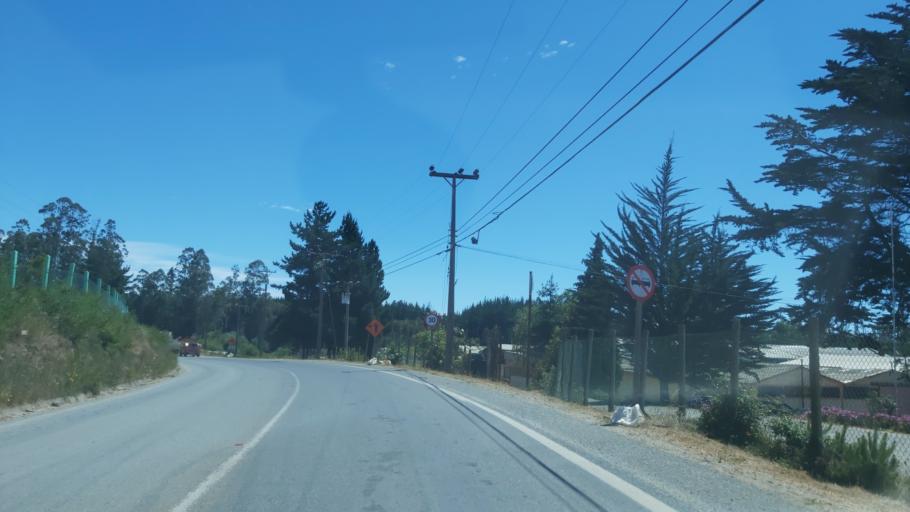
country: CL
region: Maule
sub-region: Provincia de Talca
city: Constitucion
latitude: -35.3749
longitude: -72.4189
